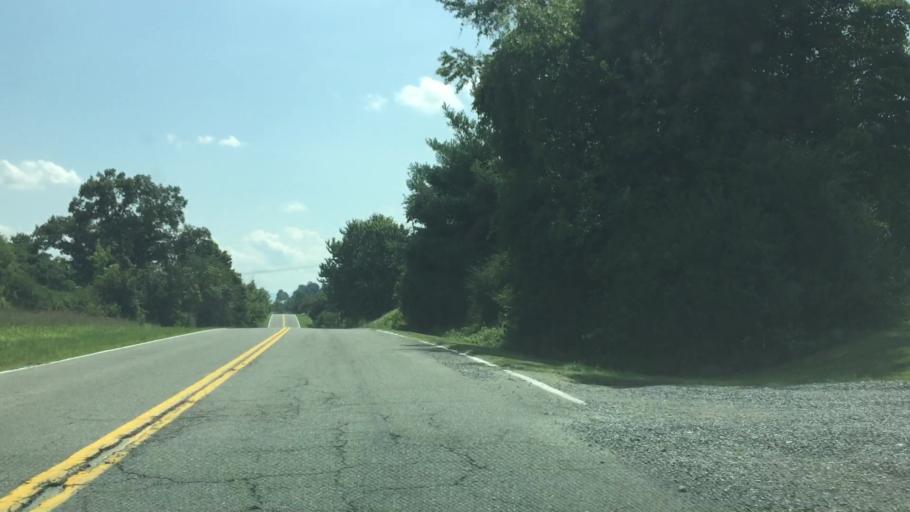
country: US
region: Virginia
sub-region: Pulaski County
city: Pulaski
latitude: 36.9737
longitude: -80.8449
